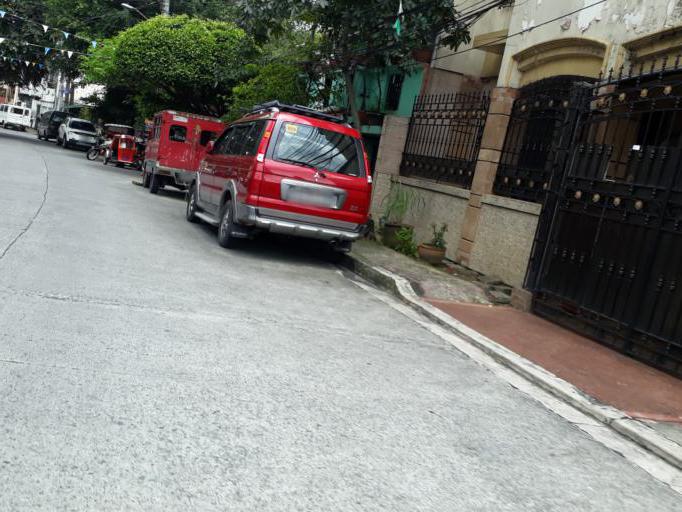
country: PH
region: Calabarzon
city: Bagong Pagasa
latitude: 14.6649
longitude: 121.0345
